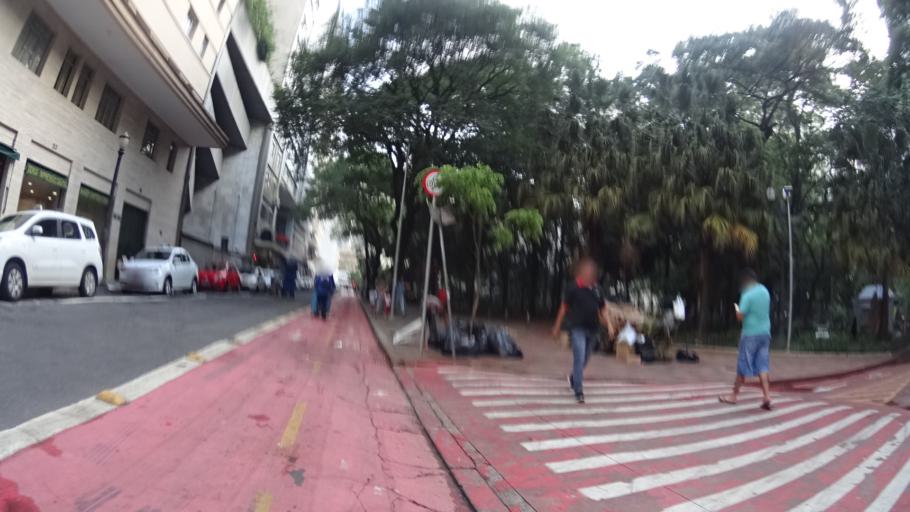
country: BR
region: Sao Paulo
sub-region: Sao Paulo
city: Sao Paulo
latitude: -23.5464
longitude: -46.6415
